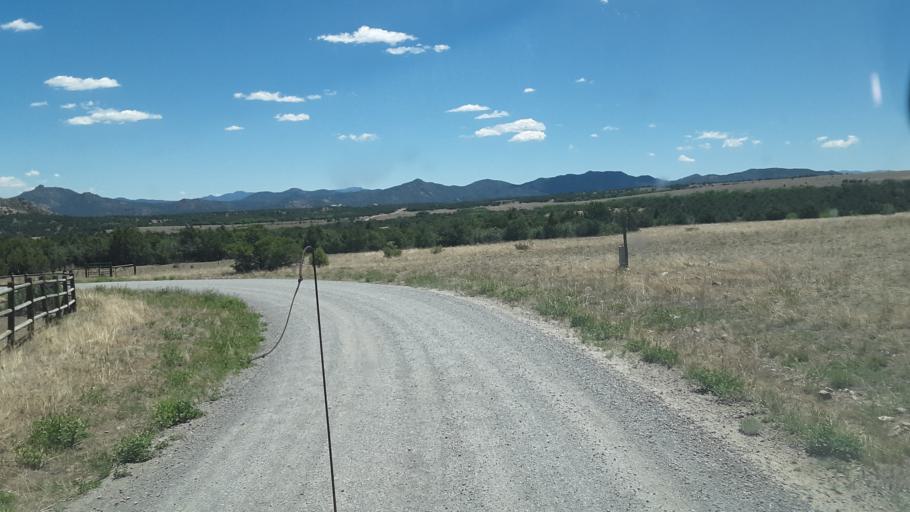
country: US
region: Colorado
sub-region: Custer County
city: Westcliffe
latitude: 38.3117
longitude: -105.6712
